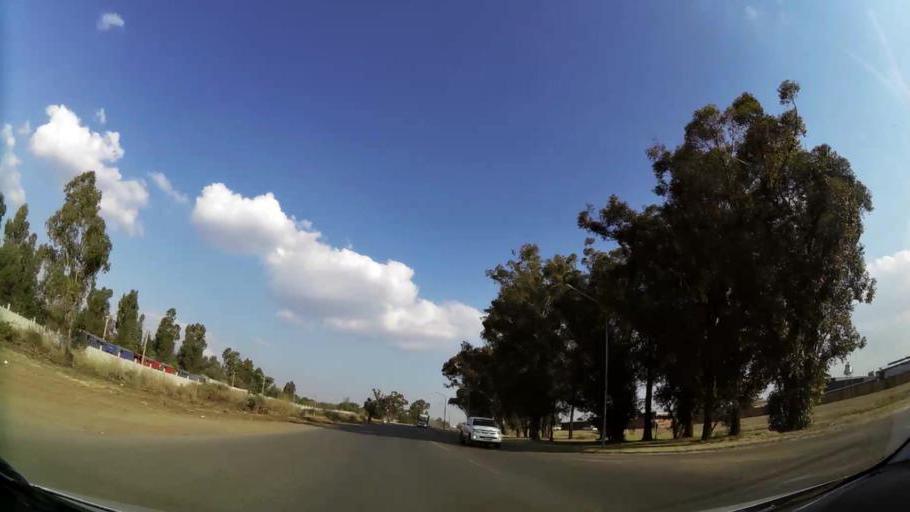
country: ZA
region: Gauteng
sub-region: Ekurhuleni Metropolitan Municipality
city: Tembisa
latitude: -25.9472
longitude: 28.2333
